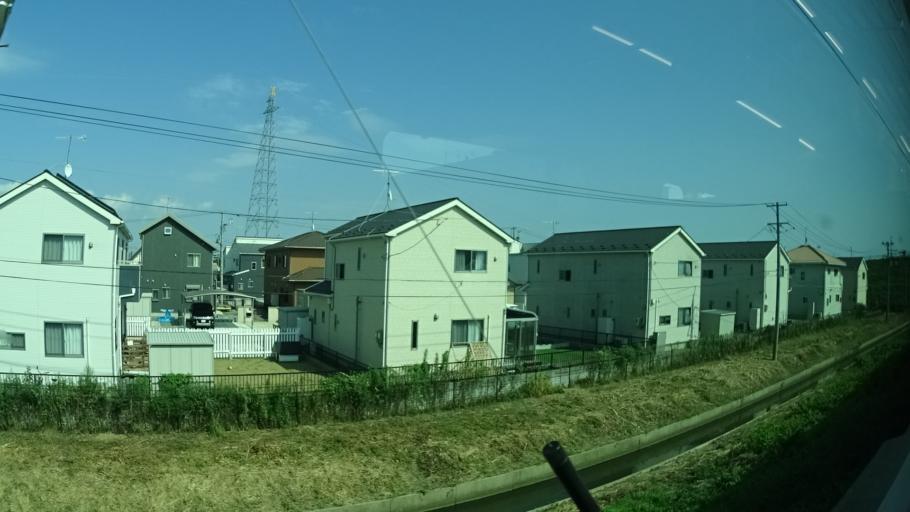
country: JP
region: Miyagi
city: Wakuya
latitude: 38.4800
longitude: 141.0990
